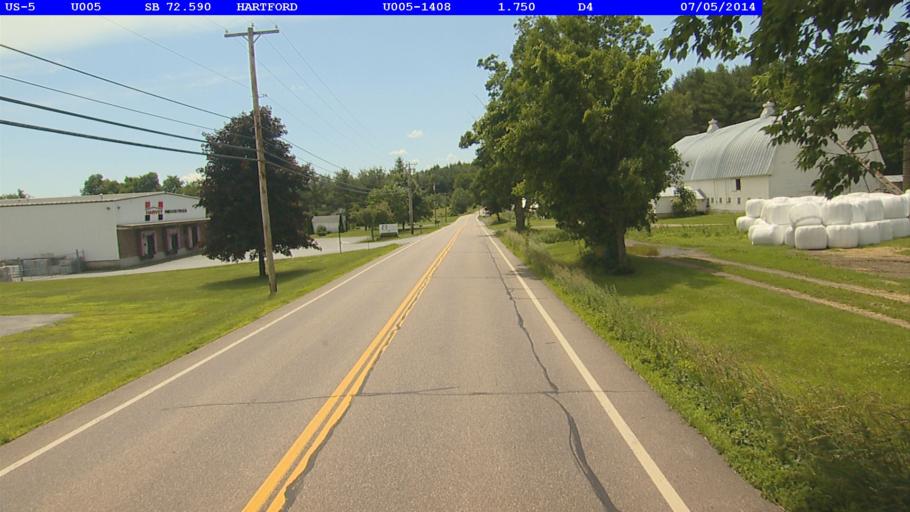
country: US
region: Vermont
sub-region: Windsor County
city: White River Junction
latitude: 43.6352
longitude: -72.3492
